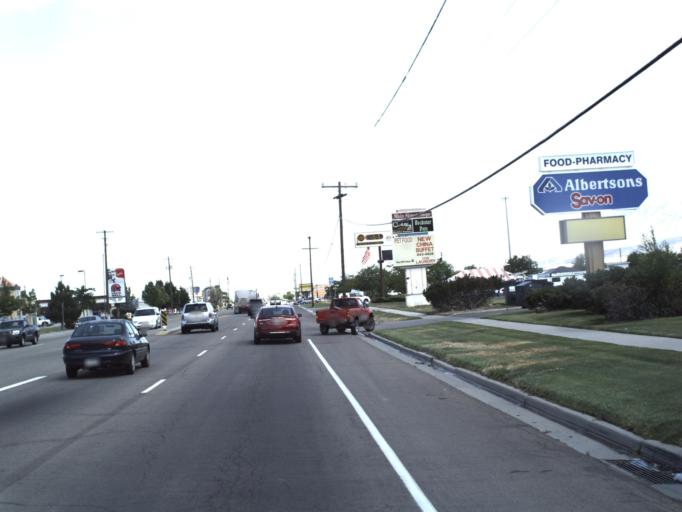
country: US
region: Utah
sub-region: Tooele County
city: Tooele
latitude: 40.5415
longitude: -112.2983
